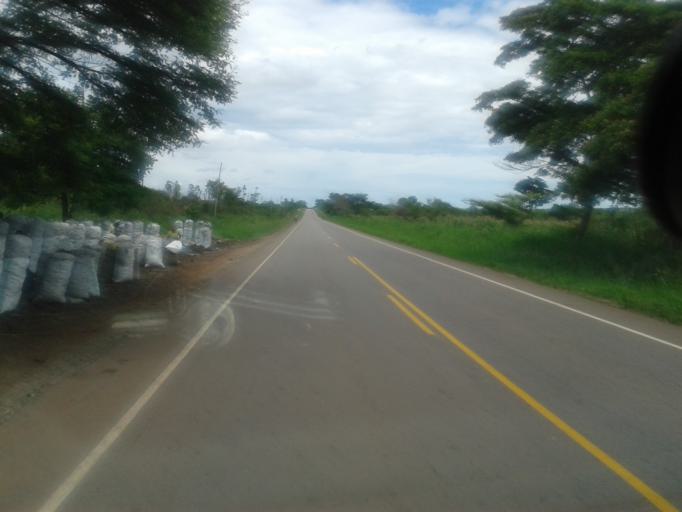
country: UG
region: Western Region
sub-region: Kiryandongo District
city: Masindi Port
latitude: 1.7345
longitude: 32.0247
